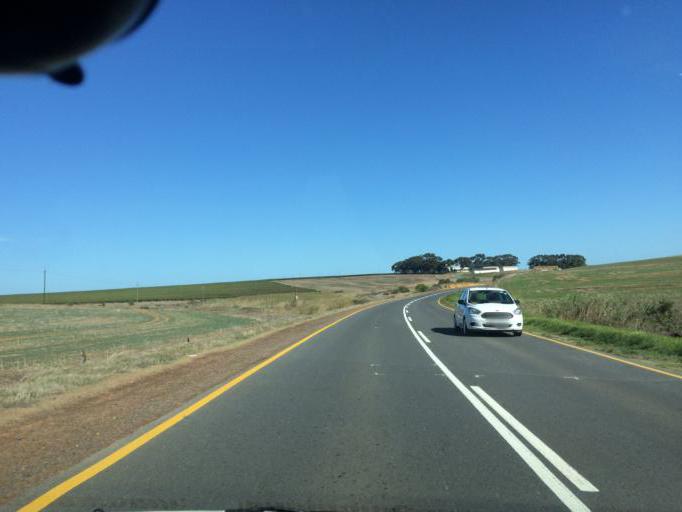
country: ZA
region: Western Cape
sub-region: City of Cape Town
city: Atlantis
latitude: -33.6665
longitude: 18.5690
